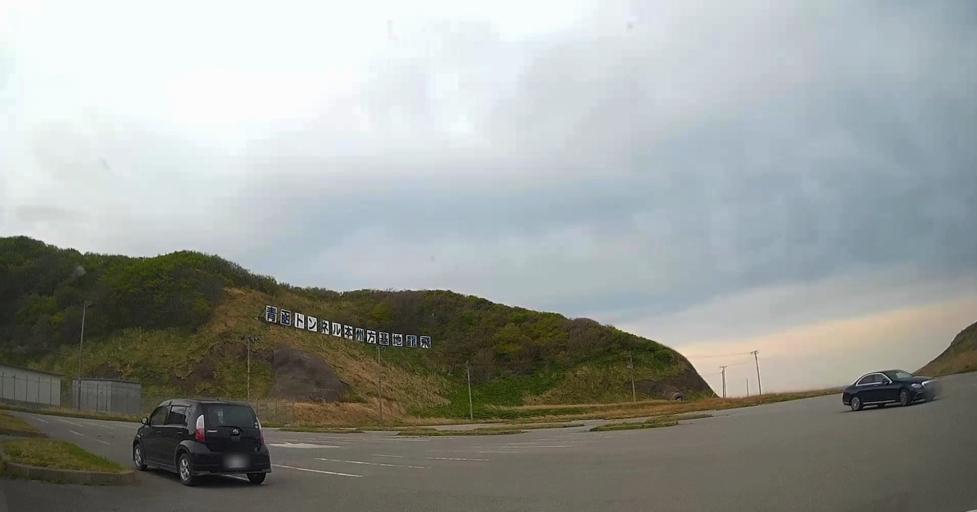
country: JP
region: Aomori
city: Shimokizukuri
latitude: 41.2530
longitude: 140.3467
